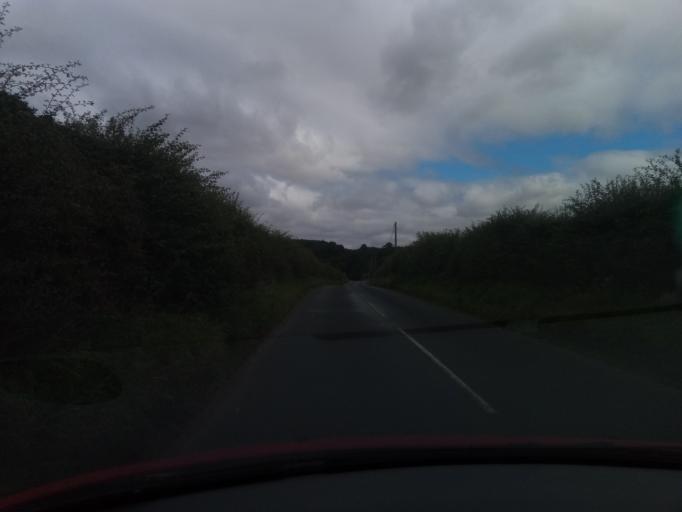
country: GB
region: Scotland
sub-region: The Scottish Borders
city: Kelso
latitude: 55.5341
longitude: -2.4529
